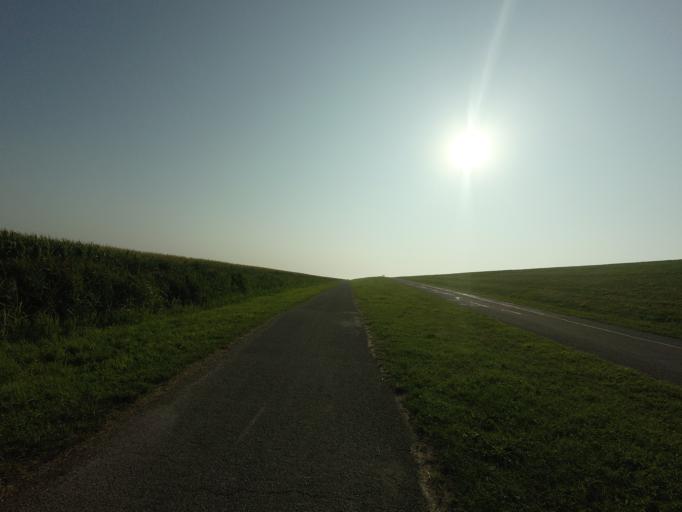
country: NL
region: Friesland
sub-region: Gemeente Schiermonnikoog
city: Schiermonnikoog
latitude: 53.4726
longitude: 6.1617
